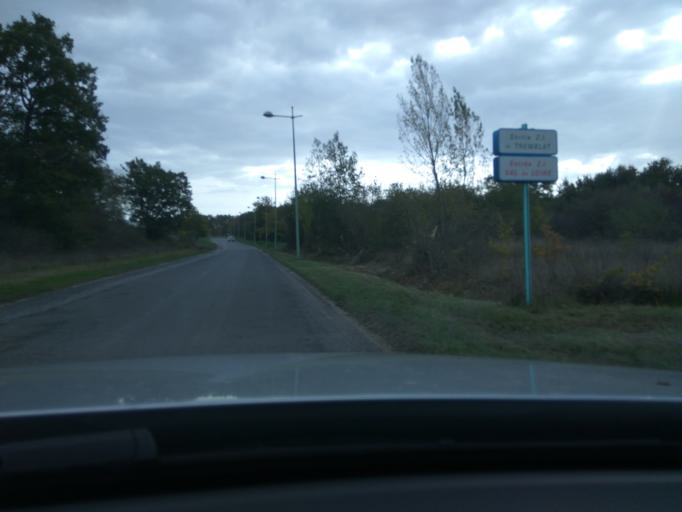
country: FR
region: Bourgogne
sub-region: Departement de la Nievre
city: Cosne-Cours-sur-Loire
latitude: 47.3794
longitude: 2.9087
